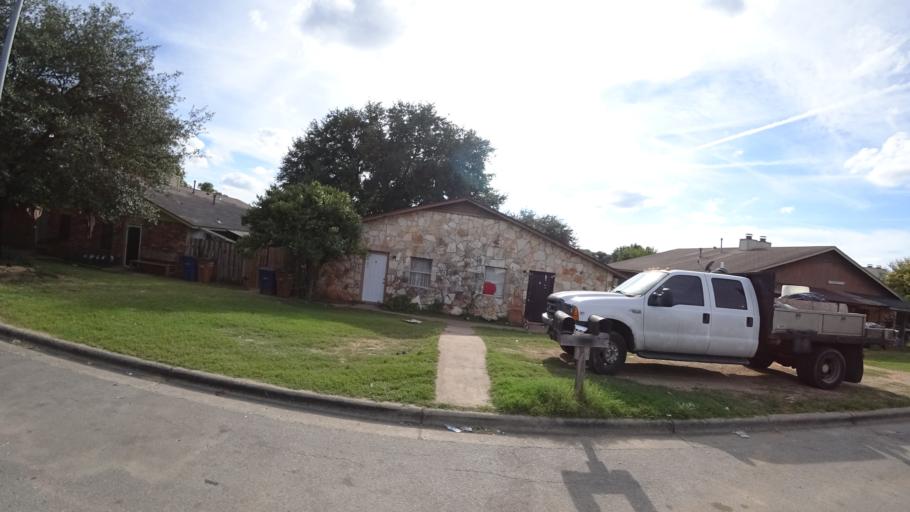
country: US
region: Texas
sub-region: Travis County
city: Onion Creek
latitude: 30.1962
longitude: -97.7580
